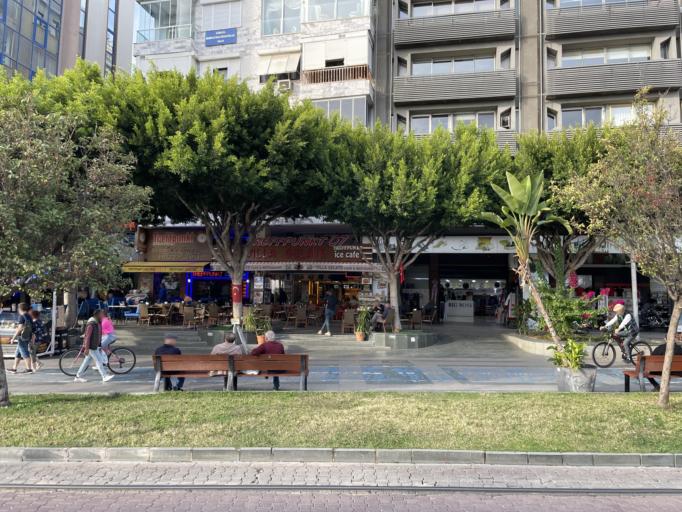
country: TR
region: Antalya
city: Antalya
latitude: 36.8872
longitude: 30.7041
